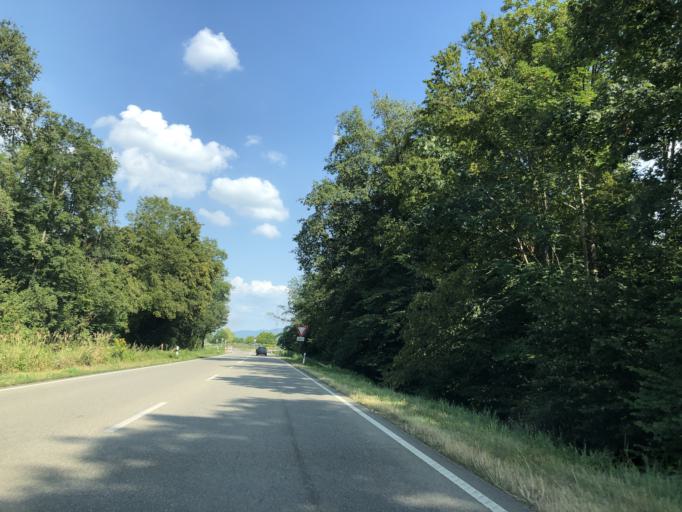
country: DE
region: Baden-Wuerttemberg
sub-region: Freiburg Region
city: Willstatt
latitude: 48.4950
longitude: 7.8182
